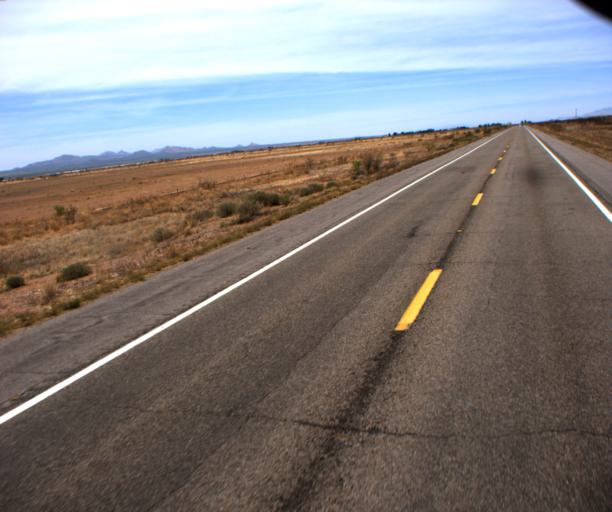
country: US
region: Arizona
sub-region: Cochise County
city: Pirtleville
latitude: 31.5722
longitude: -109.6681
